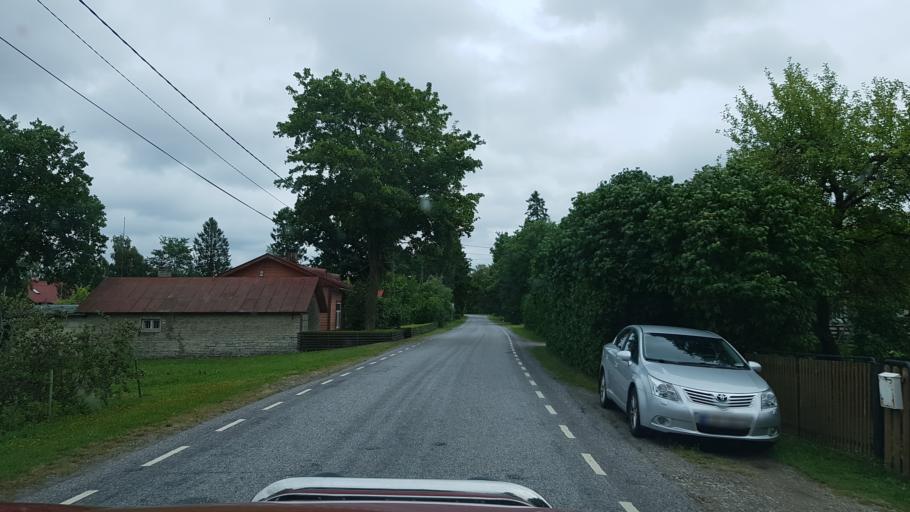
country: EE
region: Ida-Virumaa
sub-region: Puessi linn
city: Pussi
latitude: 59.3827
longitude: 27.0356
